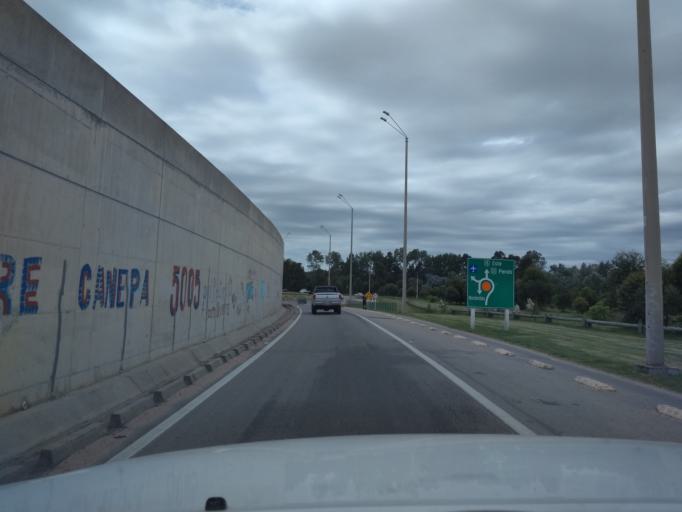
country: UY
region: Canelones
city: Barra de Carrasco
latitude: -34.8419
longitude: -56.0138
